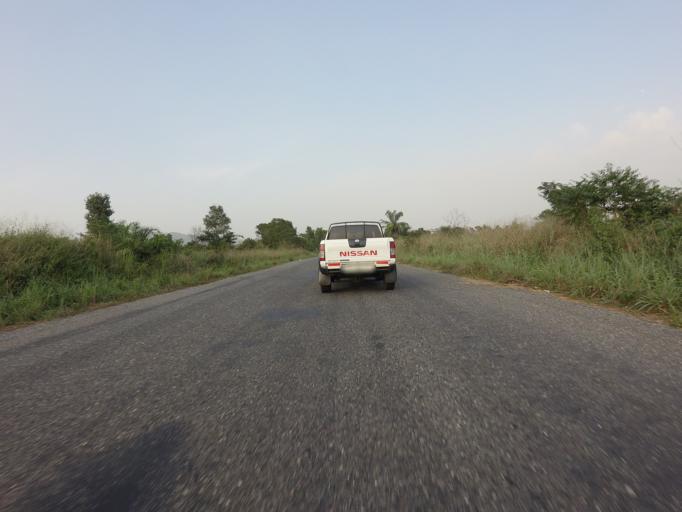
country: GH
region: Volta
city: Ho
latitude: 6.4695
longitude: 0.2261
